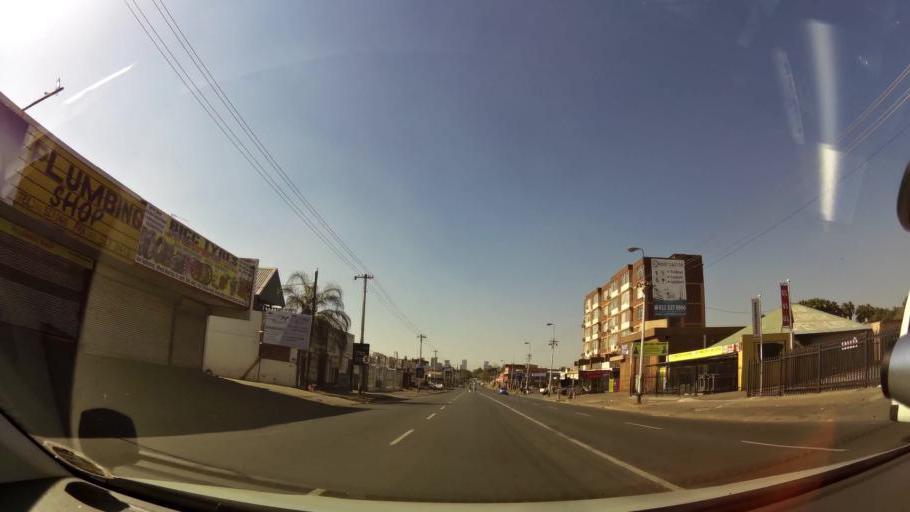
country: ZA
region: Gauteng
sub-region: City of Tshwane Metropolitan Municipality
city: Pretoria
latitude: -25.7488
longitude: 28.1532
